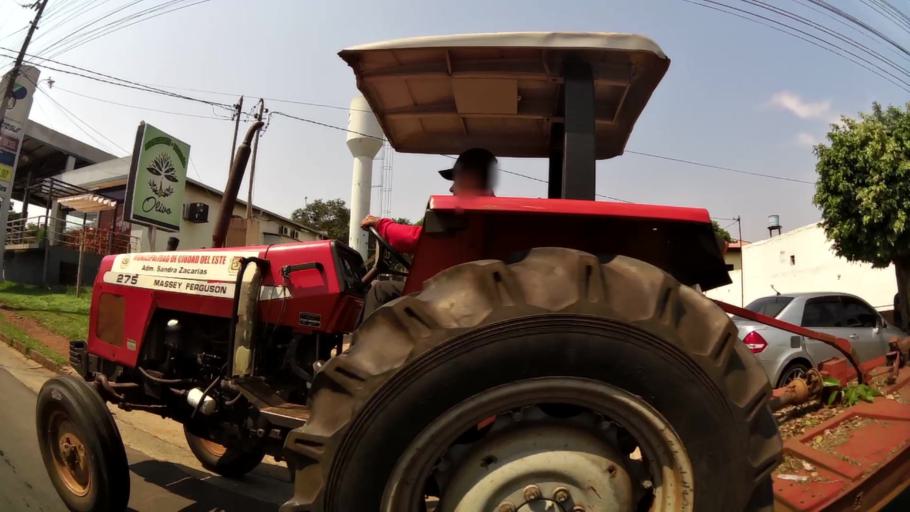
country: PY
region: Alto Parana
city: Presidente Franco
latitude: -25.5250
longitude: -54.6232
